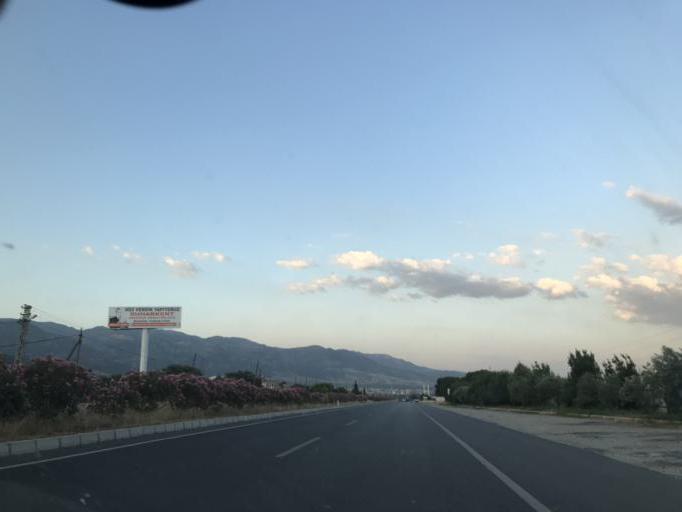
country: TR
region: Aydin
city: Buharkent
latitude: 37.9550
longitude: 28.6969
